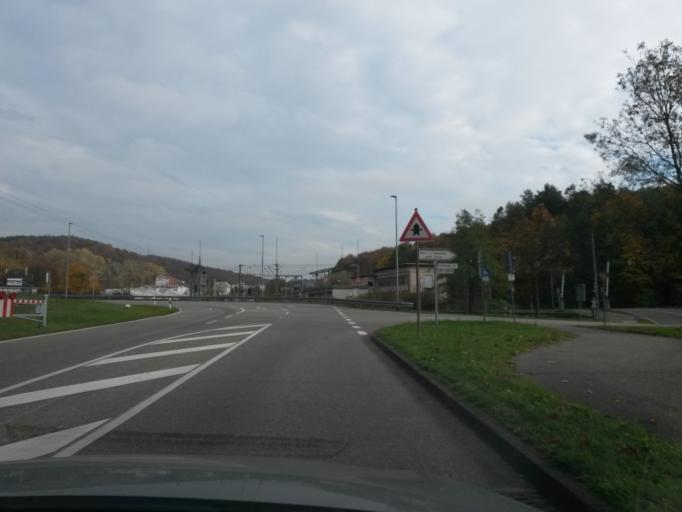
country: DE
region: Baden-Wuerttemberg
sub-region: Karlsruhe Region
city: Ettlingen
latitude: 48.9352
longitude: 8.4314
